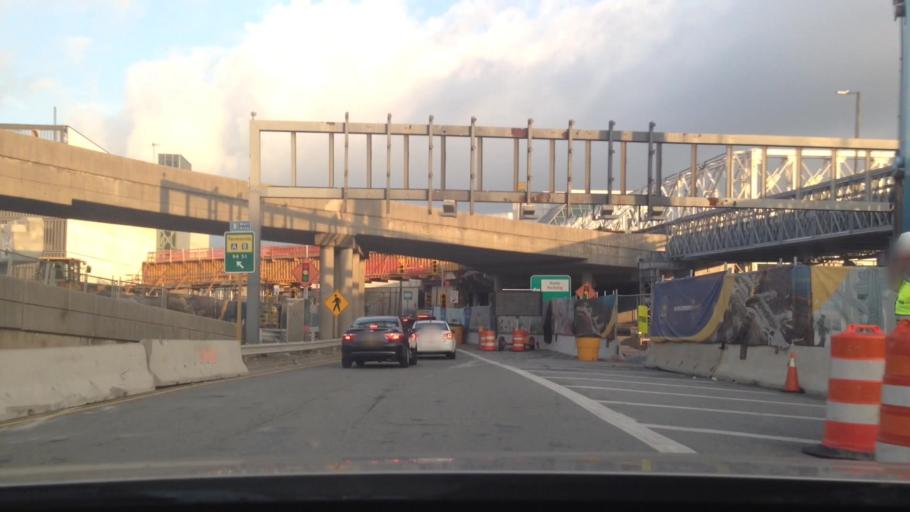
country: US
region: New York
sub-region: Bronx
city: The Bronx
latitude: 40.7692
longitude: -73.8636
